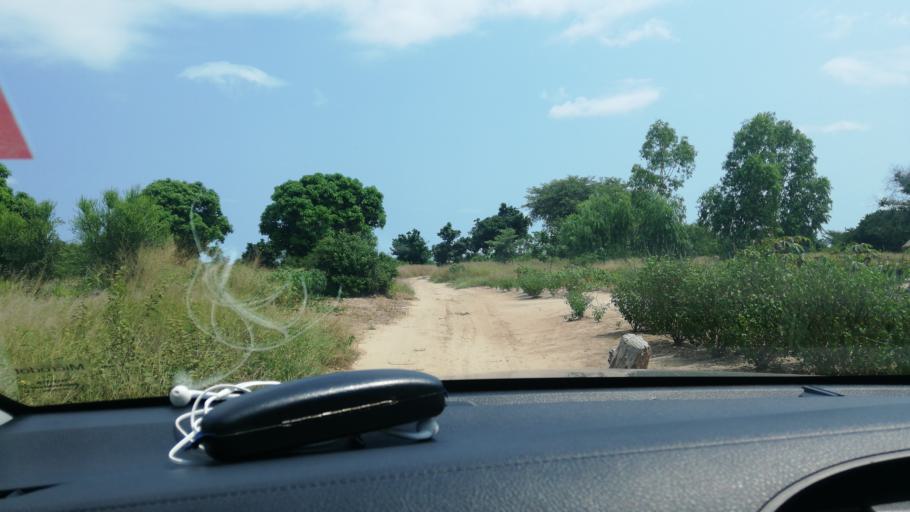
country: MZ
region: Maputo
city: Matola
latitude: -26.1104
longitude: 32.4285
